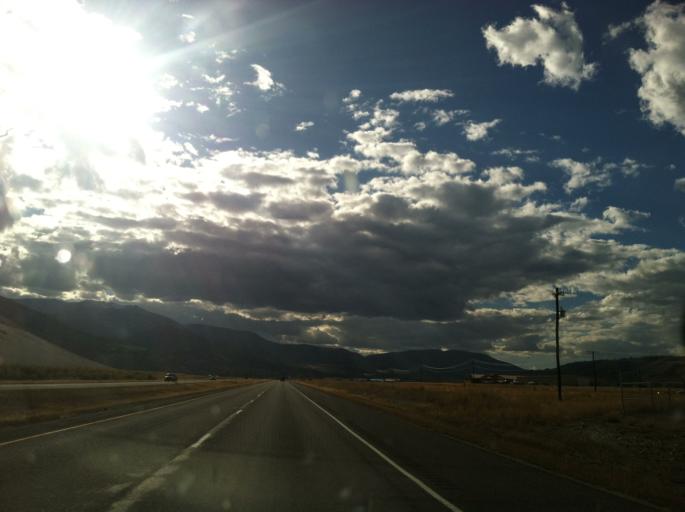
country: US
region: Montana
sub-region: Deer Lodge County
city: Anaconda
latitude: 46.1275
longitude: -112.9109
